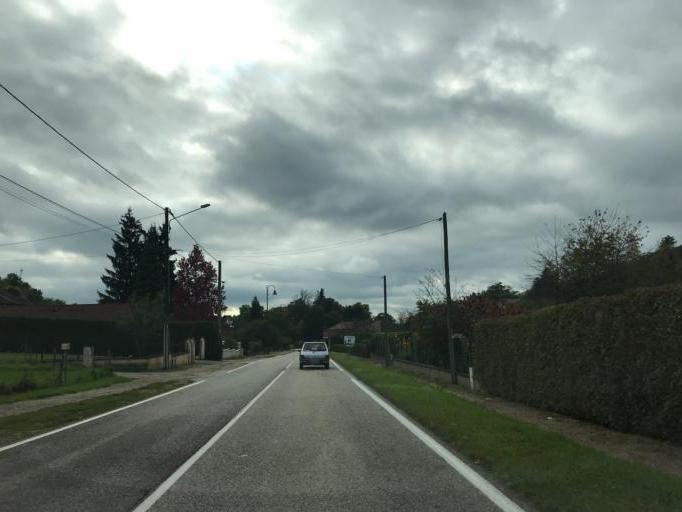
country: FR
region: Rhone-Alpes
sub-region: Departement de l'Ain
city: Jasseron
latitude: 46.2143
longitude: 5.3348
